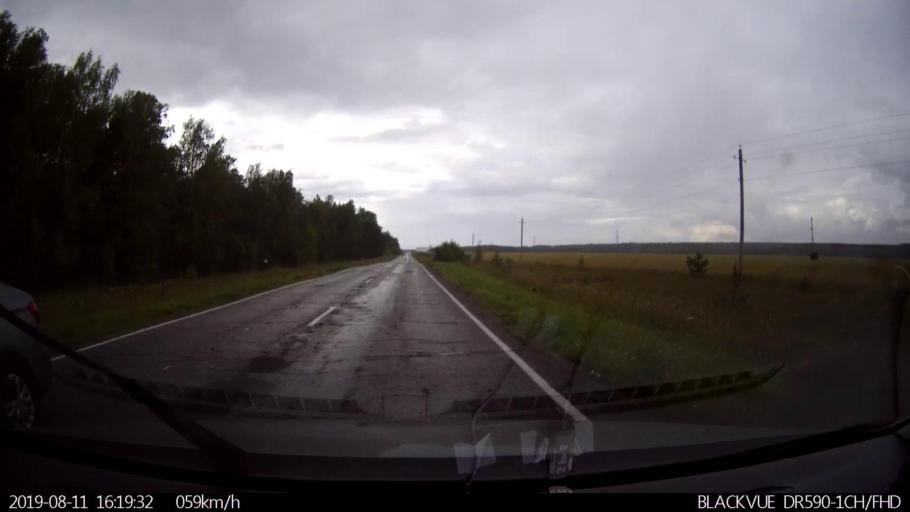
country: RU
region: Ulyanovsk
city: Mayna
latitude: 54.0645
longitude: 47.6069
